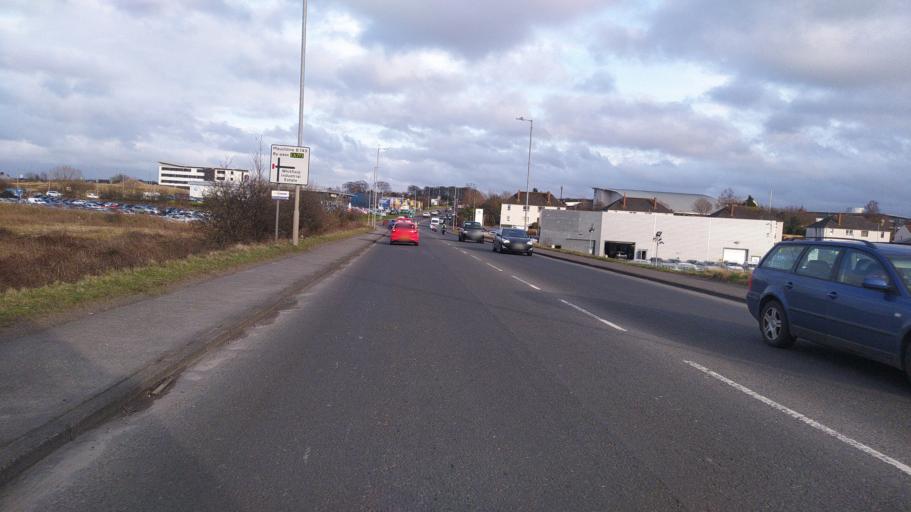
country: GB
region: Scotland
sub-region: South Ayrshire
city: Prestwick
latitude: 55.4773
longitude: -4.5928
